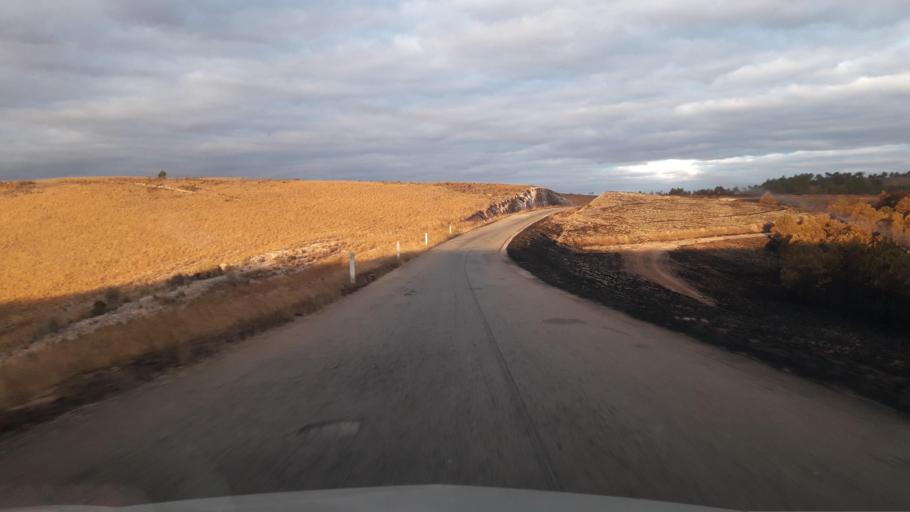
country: MG
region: Analamanga
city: Ankazobe
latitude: -17.8786
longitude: 47.0463
